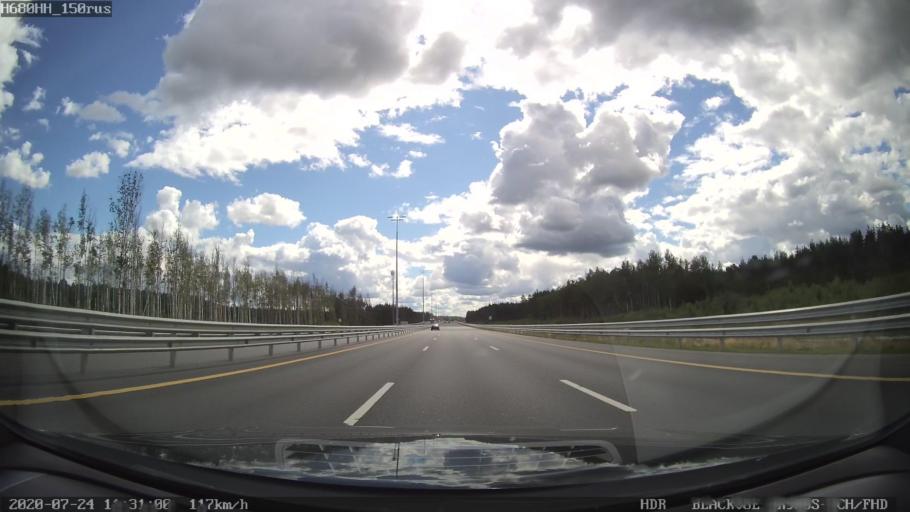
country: RU
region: Leningrad
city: Krasnyy Bor
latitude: 59.6628
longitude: 30.6241
